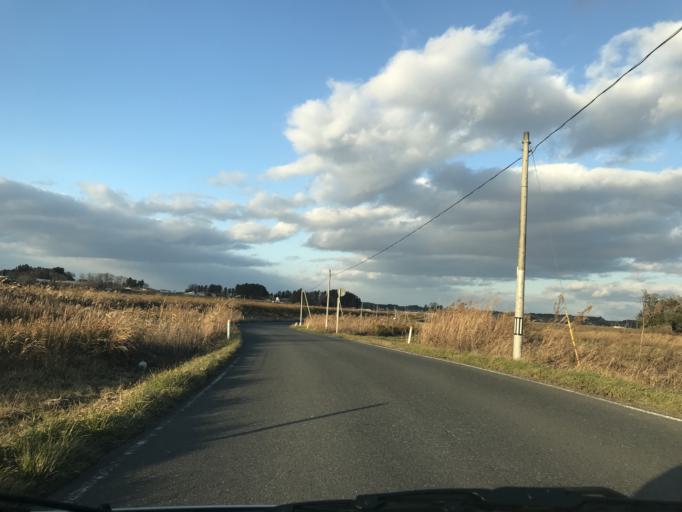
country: JP
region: Miyagi
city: Kogota
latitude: 38.6271
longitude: 141.0676
